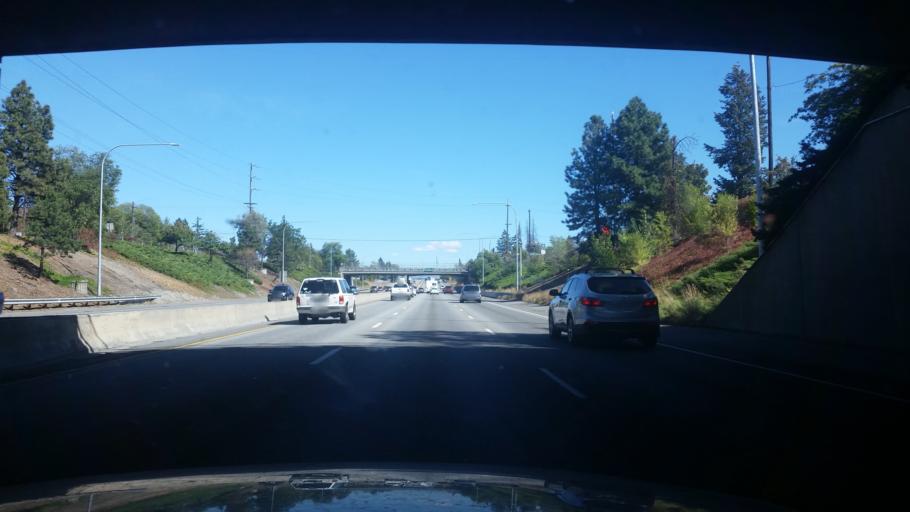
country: US
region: Washington
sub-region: Spokane County
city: Spokane
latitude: 47.6540
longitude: -117.3612
